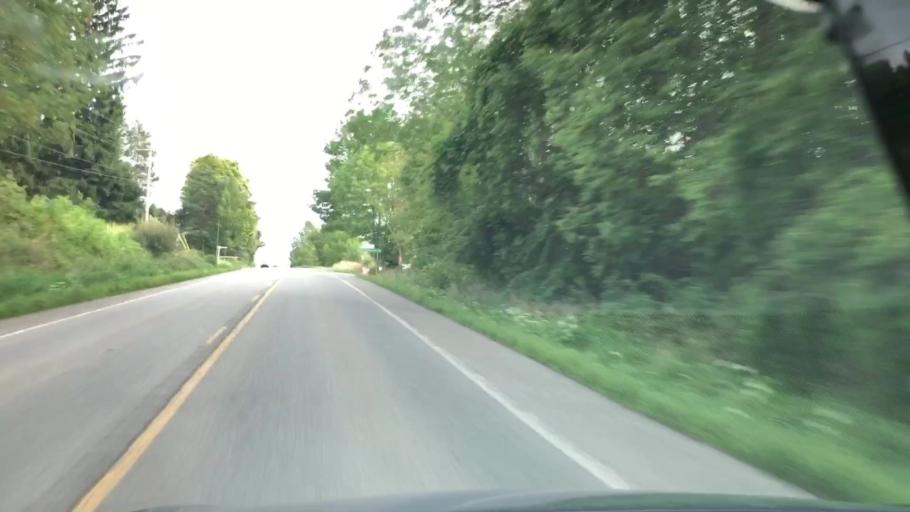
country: US
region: Pennsylvania
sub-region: Erie County
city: Union City
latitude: 41.8457
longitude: -79.8230
